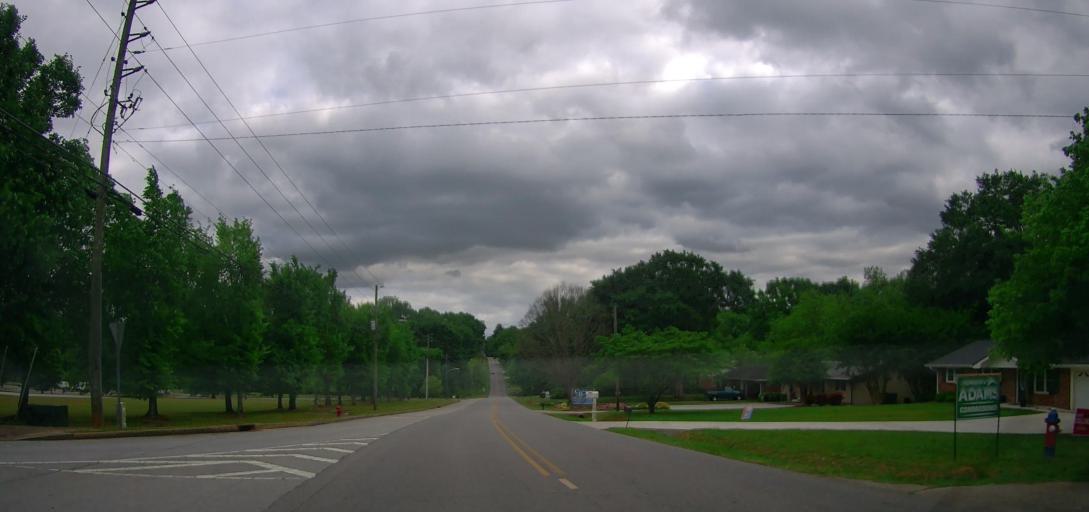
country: US
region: Georgia
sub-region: Walton County
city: Monroe
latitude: 33.7978
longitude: -83.6990
